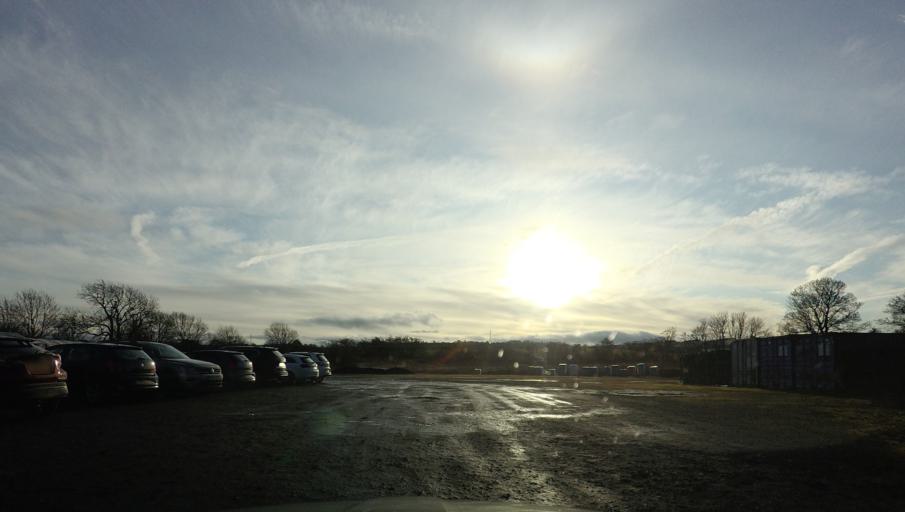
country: GB
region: Scotland
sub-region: West Lothian
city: East Calder
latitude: 55.8964
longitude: -3.4500
